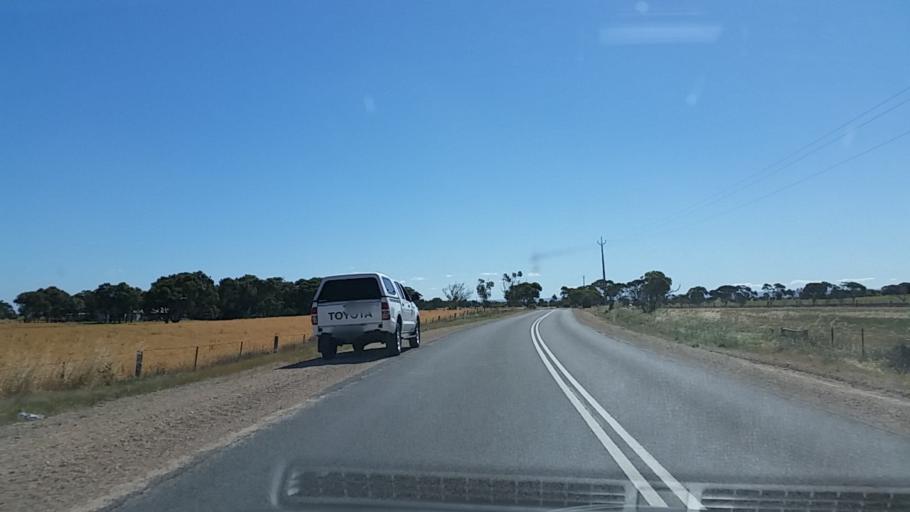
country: AU
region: South Australia
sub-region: Alexandrina
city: Langhorne Creek
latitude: -35.3156
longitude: 139.1116
